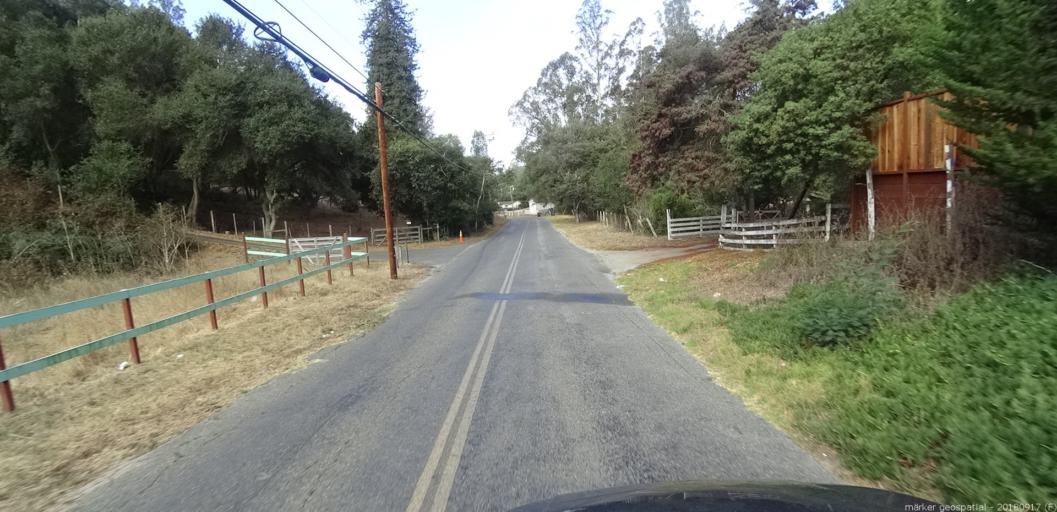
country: US
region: California
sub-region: Monterey County
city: Prunedale
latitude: 36.8187
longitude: -121.6856
